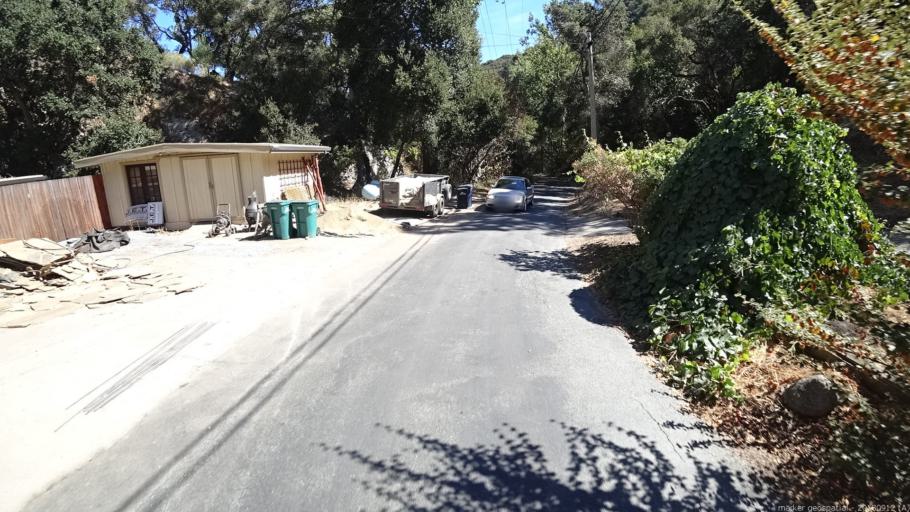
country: US
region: California
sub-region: Monterey County
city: Carmel Valley Village
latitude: 36.4636
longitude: -121.7252
